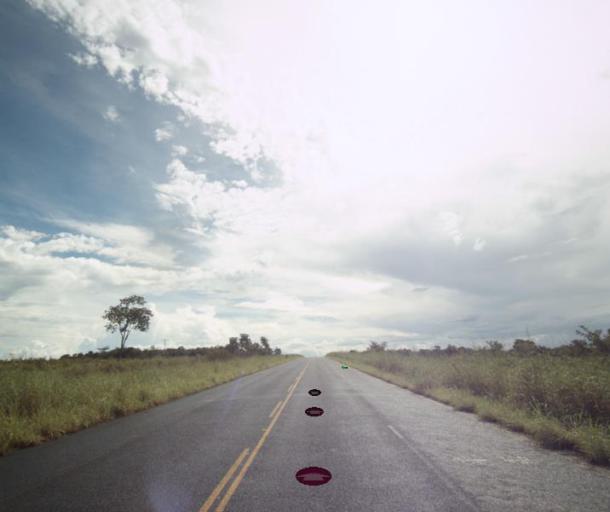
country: BR
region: Goias
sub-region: Sao Miguel Do Araguaia
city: Sao Miguel do Araguaia
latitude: -13.2975
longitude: -50.3373
